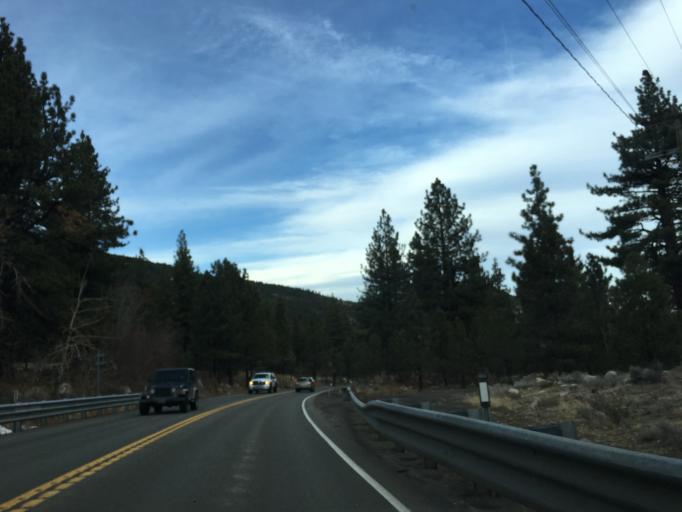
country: US
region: Nevada
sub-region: Washoe County
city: Incline Village
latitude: 39.3550
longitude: -119.8558
